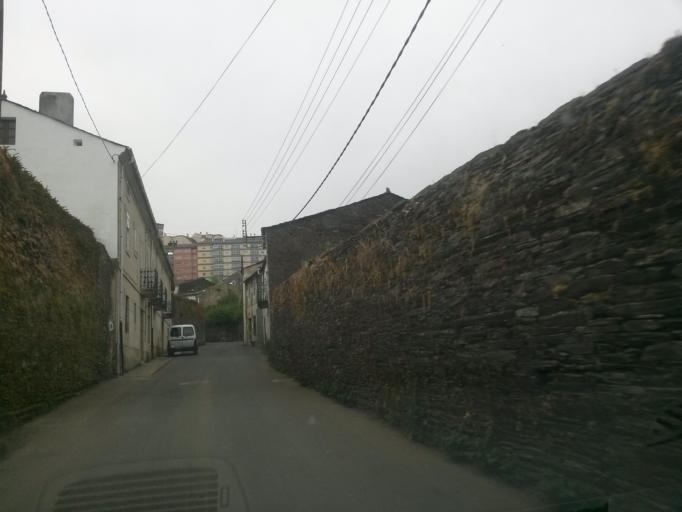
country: ES
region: Galicia
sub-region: Provincia de Lugo
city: Lugo
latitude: 43.0144
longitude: -7.5471
